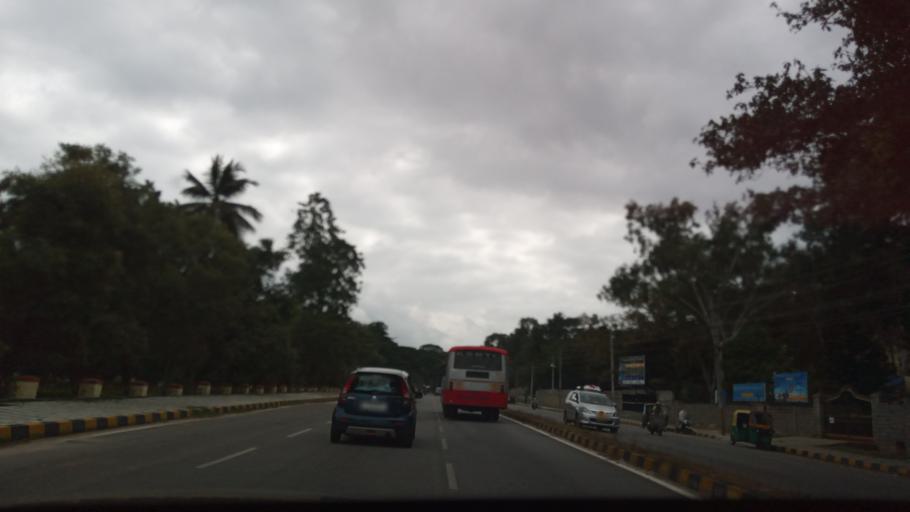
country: IN
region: Karnataka
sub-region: Mysore
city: Mysore
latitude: 12.3354
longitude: 76.6578
